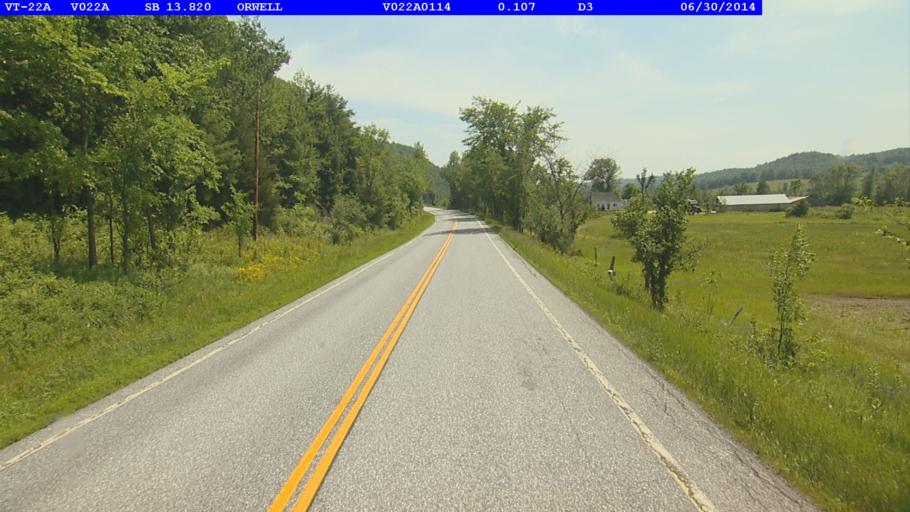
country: US
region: New York
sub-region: Essex County
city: Ticonderoga
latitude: 43.7589
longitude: -73.3120
